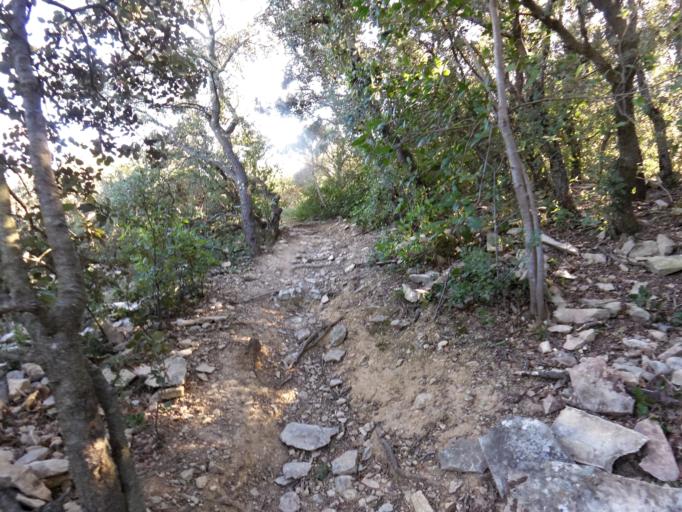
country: FR
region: Languedoc-Roussillon
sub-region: Departement du Gard
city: Clarensac
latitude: 43.8367
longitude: 4.2063
